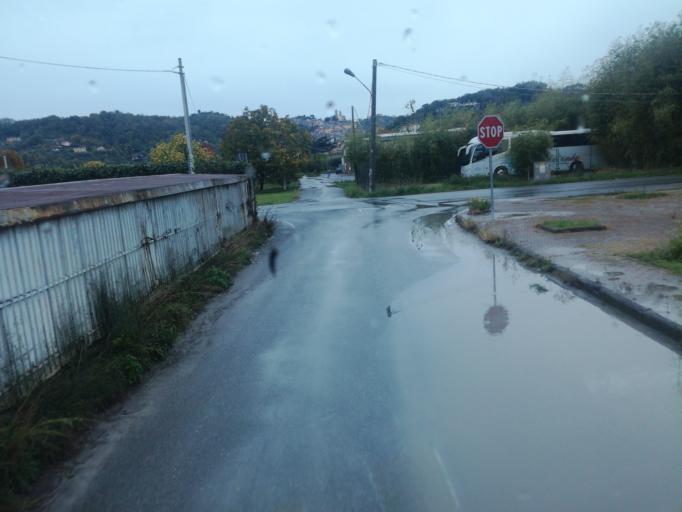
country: IT
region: Liguria
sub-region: Provincia di La Spezia
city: Arcola
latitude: 44.1210
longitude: 9.9185
